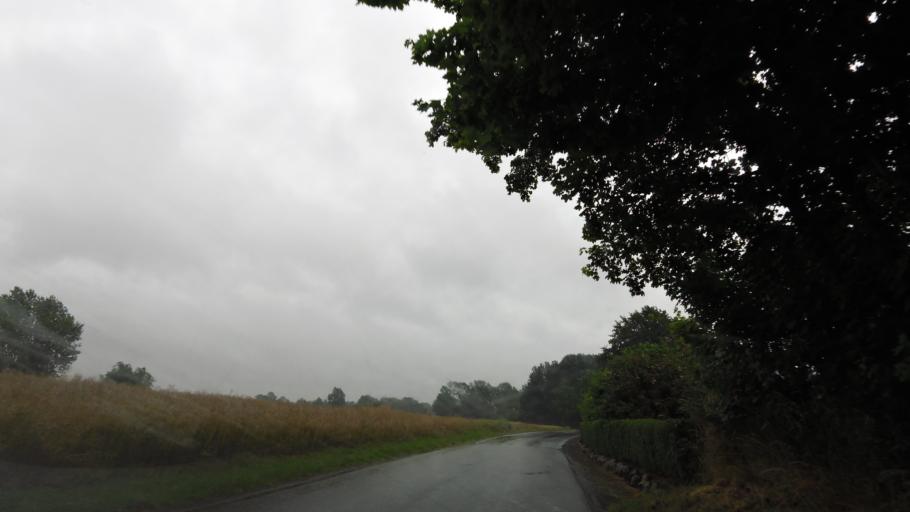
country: DK
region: South Denmark
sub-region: Nordfyns Kommune
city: Otterup
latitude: 55.5514
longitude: 10.4373
